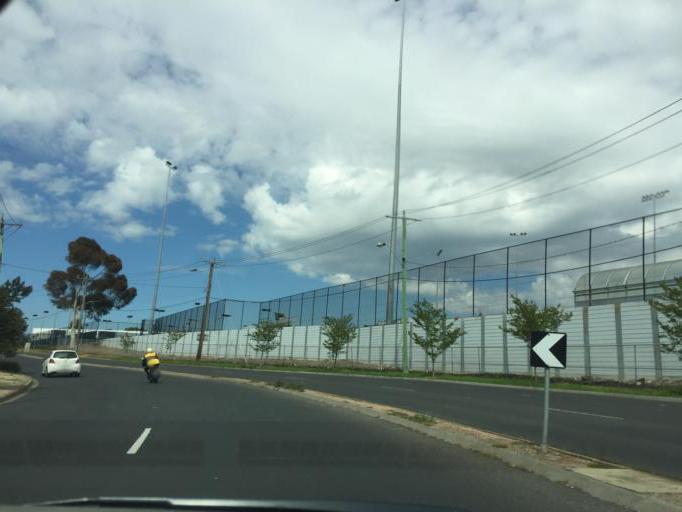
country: AU
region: Victoria
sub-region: Maribyrnong
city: Maribyrnong
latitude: -37.7766
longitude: 144.8905
